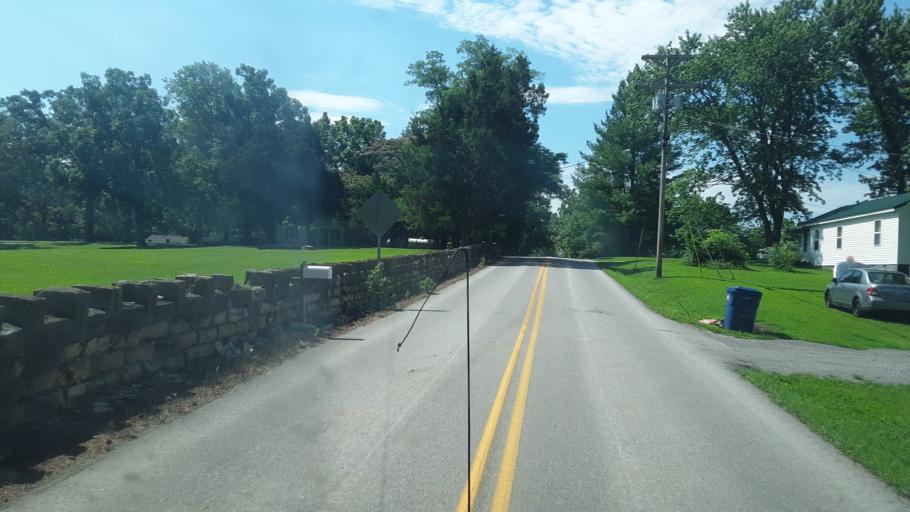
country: US
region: Kentucky
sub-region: Todd County
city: Elkton
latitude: 36.8421
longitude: -87.3009
